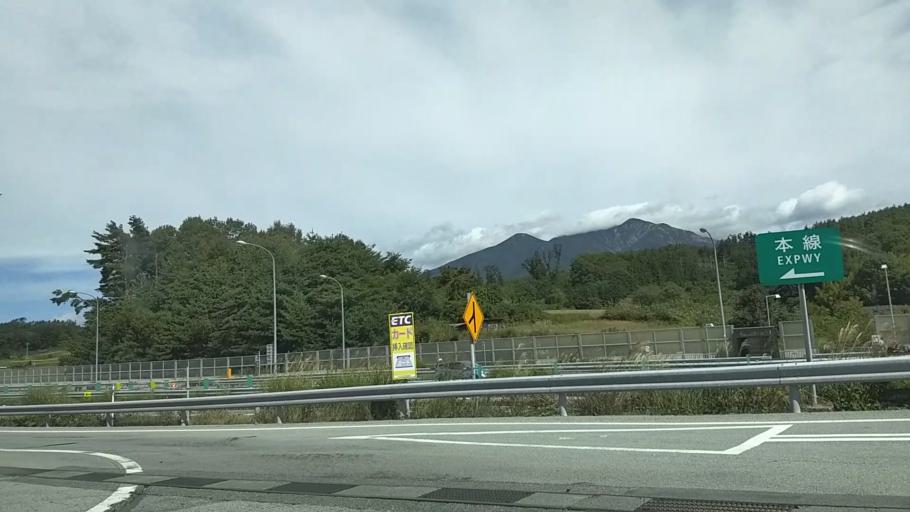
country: JP
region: Yamanashi
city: Nirasaki
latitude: 35.8452
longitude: 138.3643
